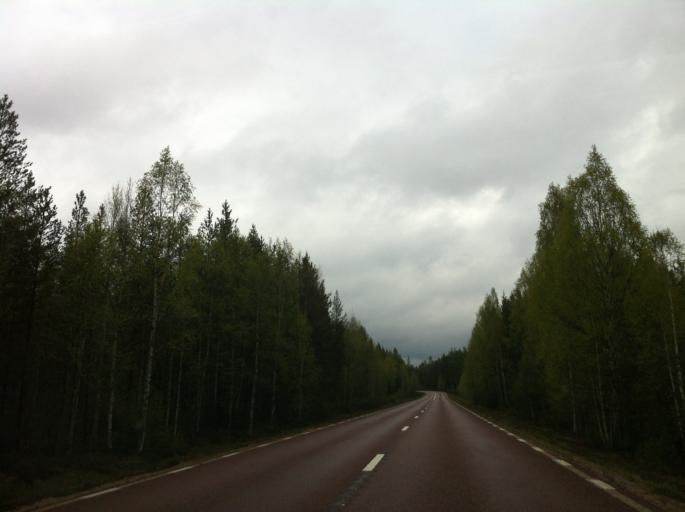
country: SE
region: Jaemtland
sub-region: Harjedalens Kommun
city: Sveg
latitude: 61.8828
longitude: 14.6275
